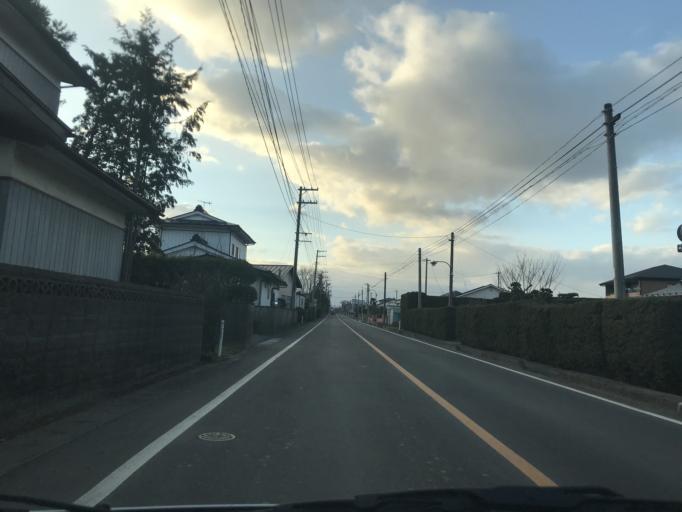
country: JP
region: Miyagi
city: Furukawa
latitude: 38.6583
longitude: 141.0188
